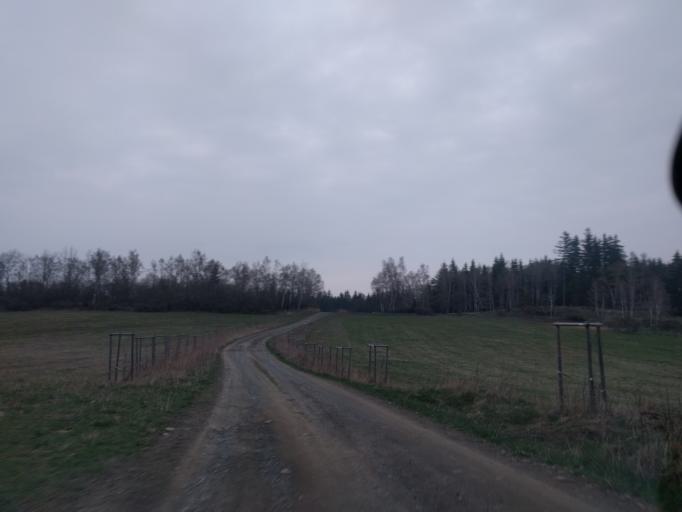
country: CZ
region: Karlovarsky
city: Bochov
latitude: 50.1031
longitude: 13.0950
